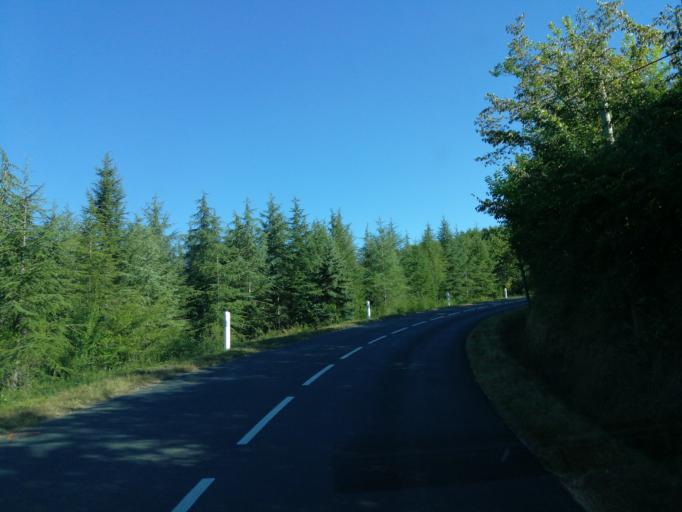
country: FR
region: Midi-Pyrenees
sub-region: Departement du Lot
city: Salviac
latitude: 44.6178
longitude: 1.2101
